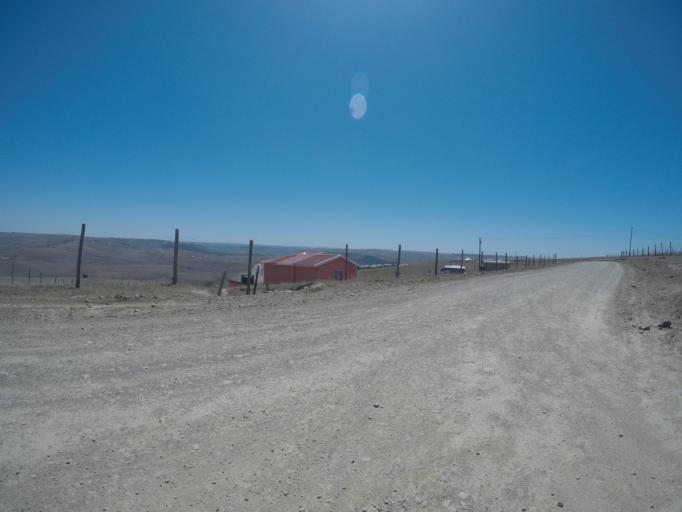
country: ZA
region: Eastern Cape
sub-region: OR Tambo District Municipality
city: Mthatha
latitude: -31.8915
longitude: 28.8773
